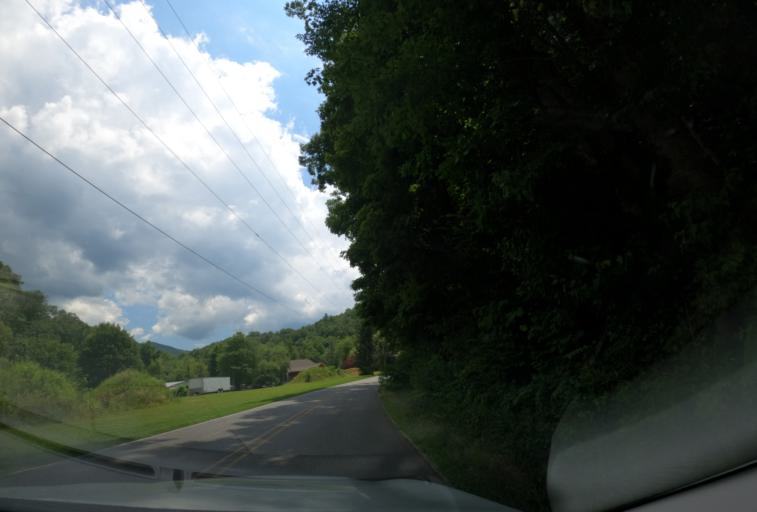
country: US
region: North Carolina
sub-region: Haywood County
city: Waynesville
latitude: 35.4289
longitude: -82.9195
